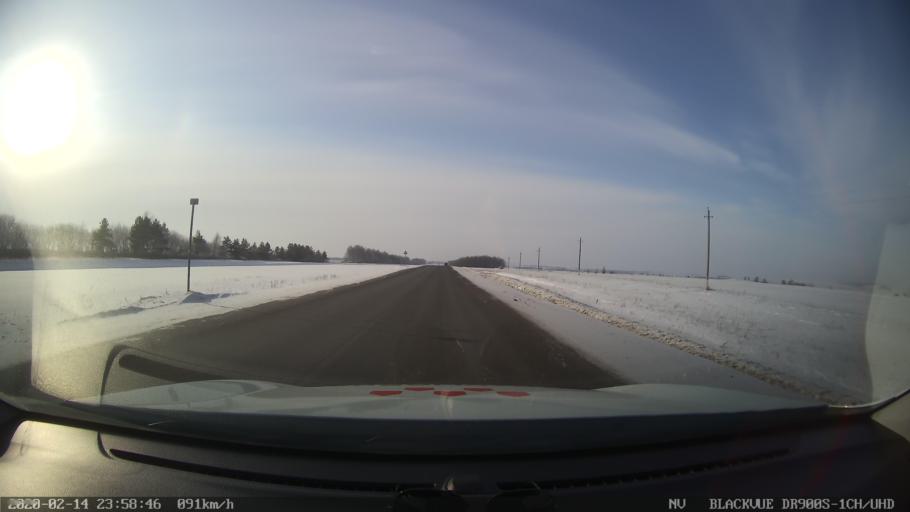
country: RU
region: Tatarstan
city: Kuybyshevskiy Zaton
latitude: 55.3420
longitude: 49.0802
